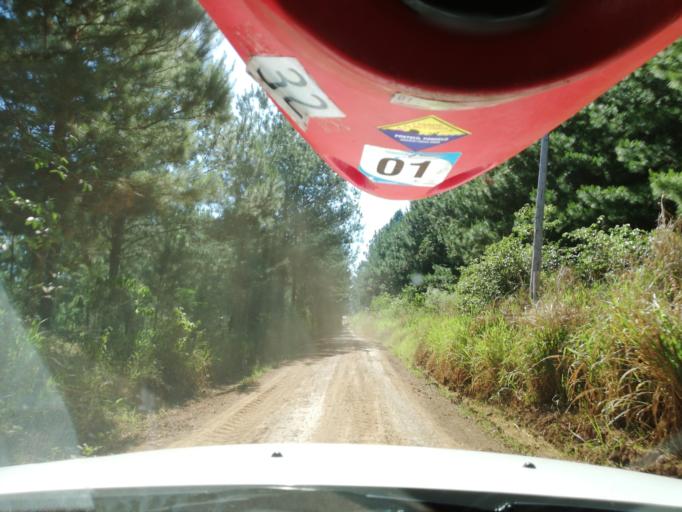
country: AR
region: Misiones
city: Puerto Leoni
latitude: -26.9688
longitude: -55.1603
